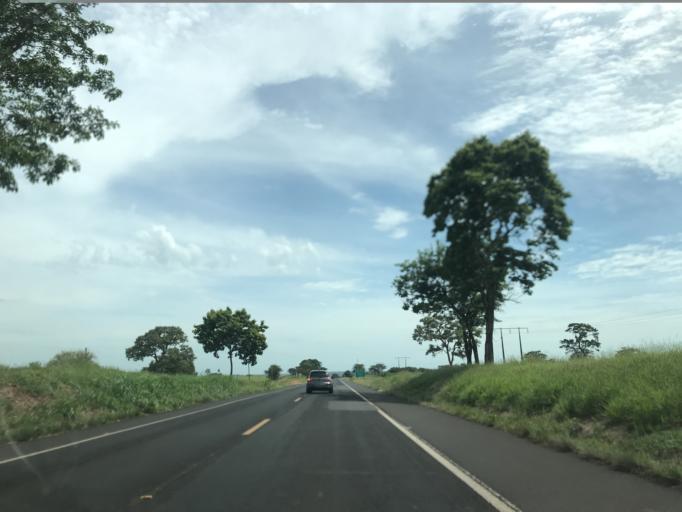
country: BR
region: Sao Paulo
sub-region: Nova Granada
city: Nova Granada
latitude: -20.3698
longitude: -49.2247
